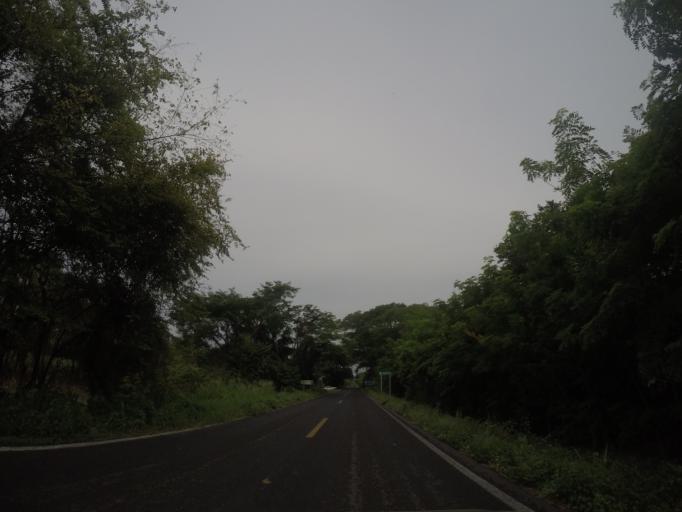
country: MX
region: Oaxaca
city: San Pedro Mixtepec
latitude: 15.9557
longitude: -97.2372
